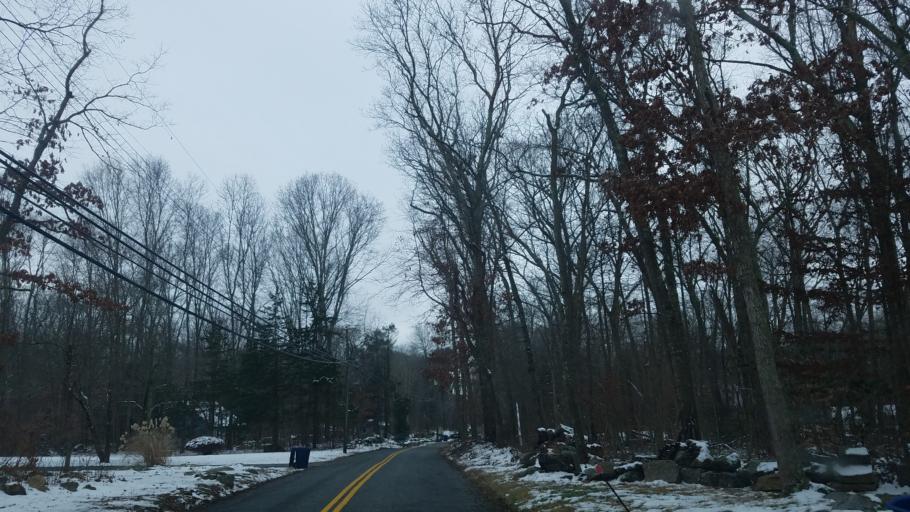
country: US
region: Connecticut
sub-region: New London County
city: Niantic
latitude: 41.3881
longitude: -72.1786
